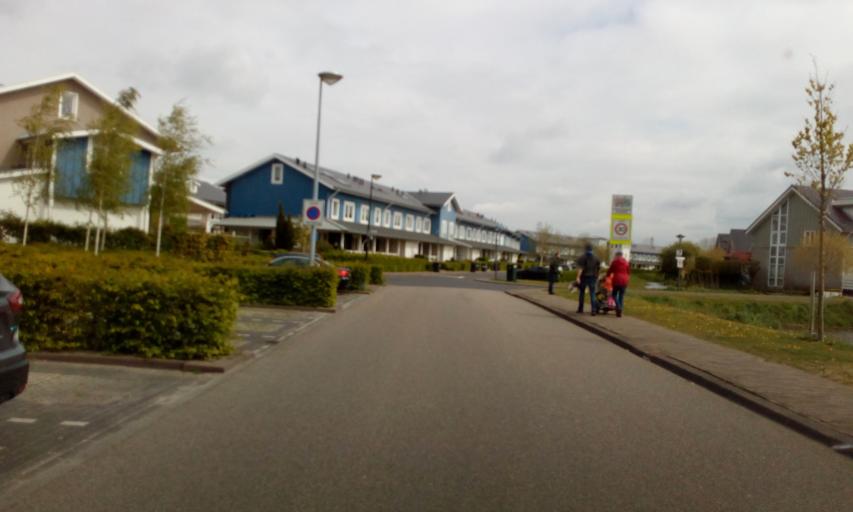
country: NL
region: South Holland
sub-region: Gemeente Schiedam
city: Schiedam
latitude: 51.9463
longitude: 4.3805
